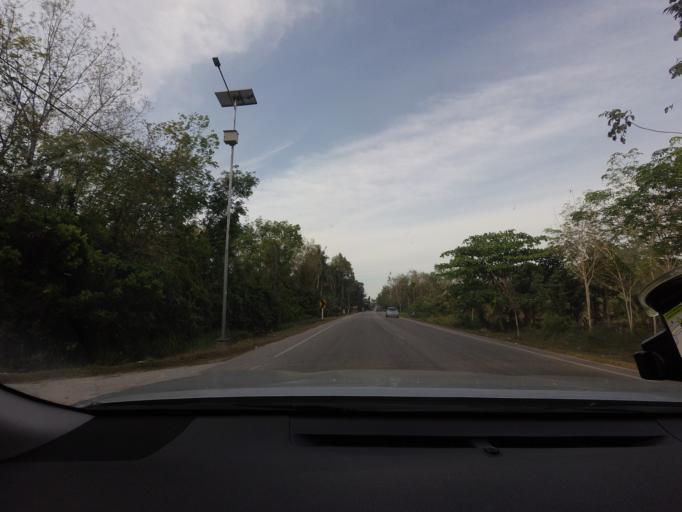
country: TH
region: Narathiwat
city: Ra-ngae
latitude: 6.3105
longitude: 101.7277
